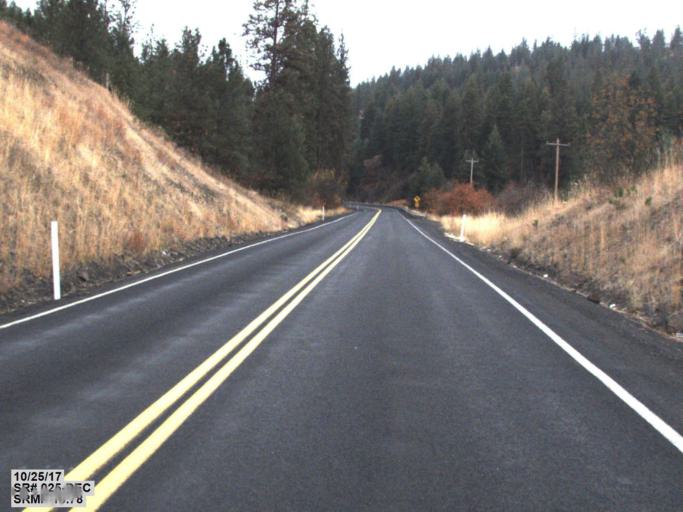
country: US
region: Washington
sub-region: Lincoln County
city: Davenport
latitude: 47.8784
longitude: -118.2665
